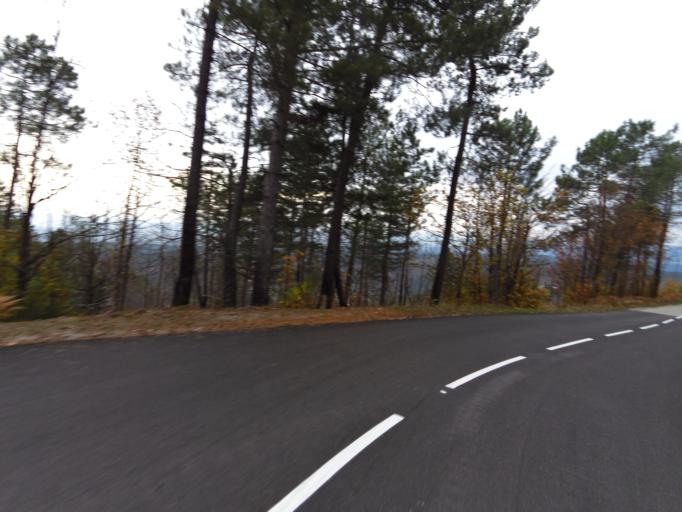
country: FR
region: Rhone-Alpes
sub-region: Departement de l'Ardeche
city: Lablachere
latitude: 44.4924
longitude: 4.1455
